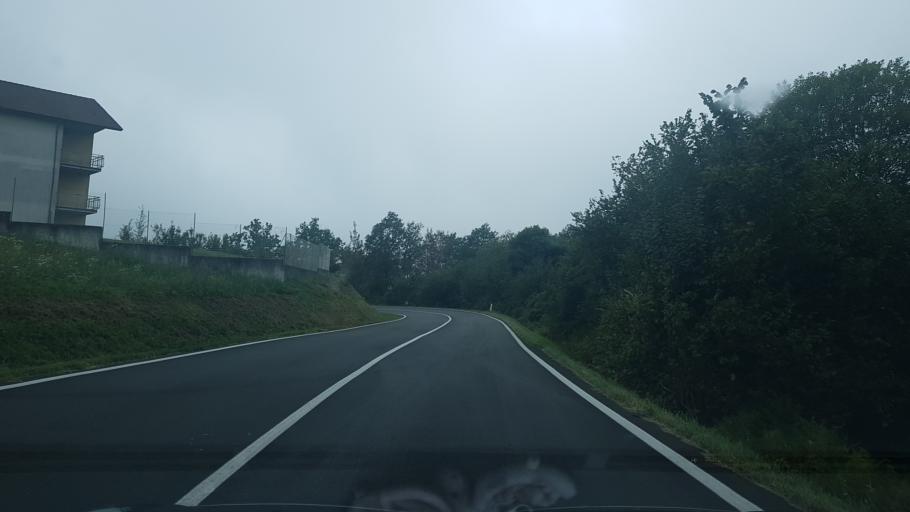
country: IT
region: Piedmont
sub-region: Provincia di Cuneo
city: Paroldo
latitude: 44.4214
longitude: 8.0929
